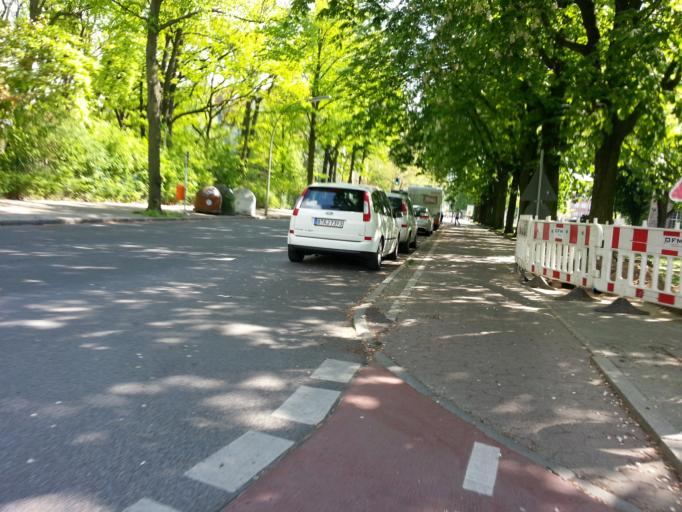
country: DE
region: Berlin
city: Siemensstadt
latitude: 52.5386
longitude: 13.2639
